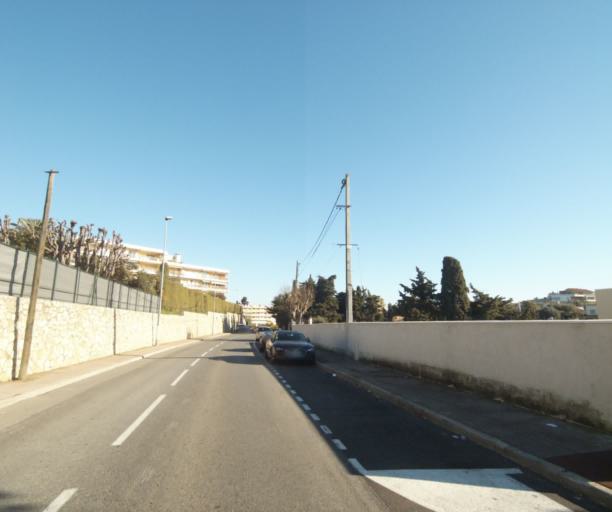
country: FR
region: Provence-Alpes-Cote d'Azur
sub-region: Departement des Alpes-Maritimes
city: Antibes
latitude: 43.5828
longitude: 7.0994
